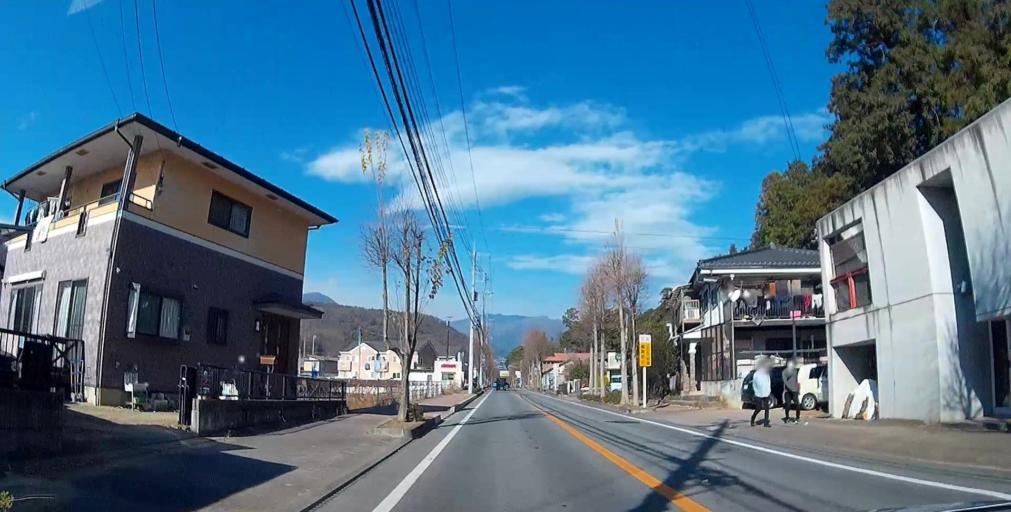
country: JP
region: Yamanashi
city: Enzan
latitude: 35.7271
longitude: 138.7138
